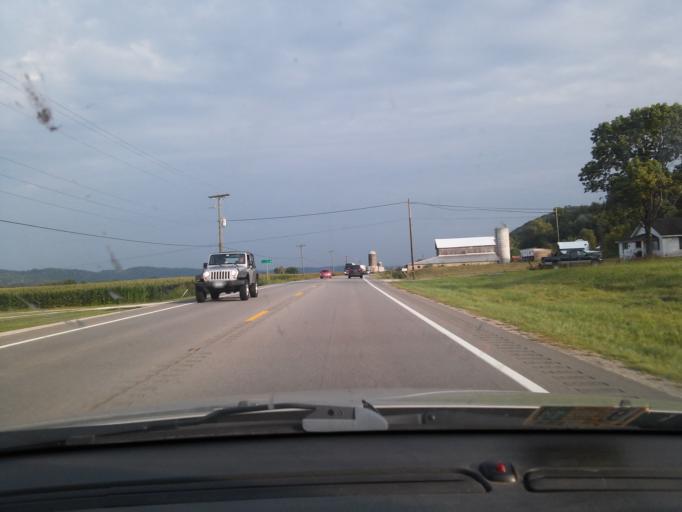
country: US
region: West Virginia
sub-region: Putnam County
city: Buffalo
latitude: 38.7401
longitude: -81.9775
